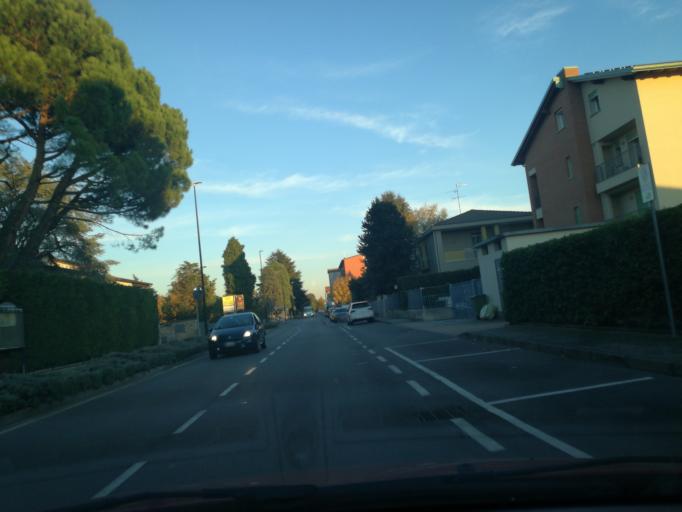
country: IT
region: Lombardy
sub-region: Provincia di Monza e Brianza
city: Bellusco
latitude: 45.6169
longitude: 9.4265
